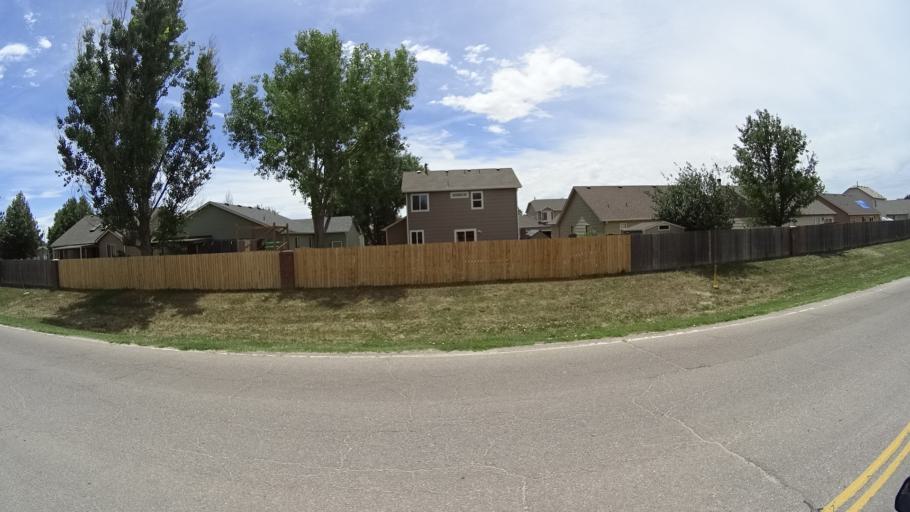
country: US
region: Colorado
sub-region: El Paso County
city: Fountain
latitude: 38.6686
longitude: -104.6772
